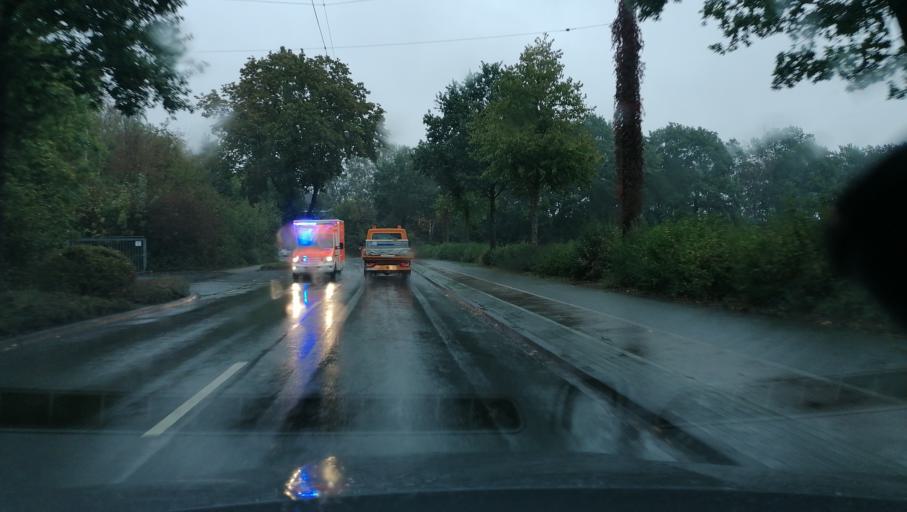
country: DE
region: North Rhine-Westphalia
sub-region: Regierungsbezirk Arnsberg
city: Herne
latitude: 51.5790
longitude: 7.2486
